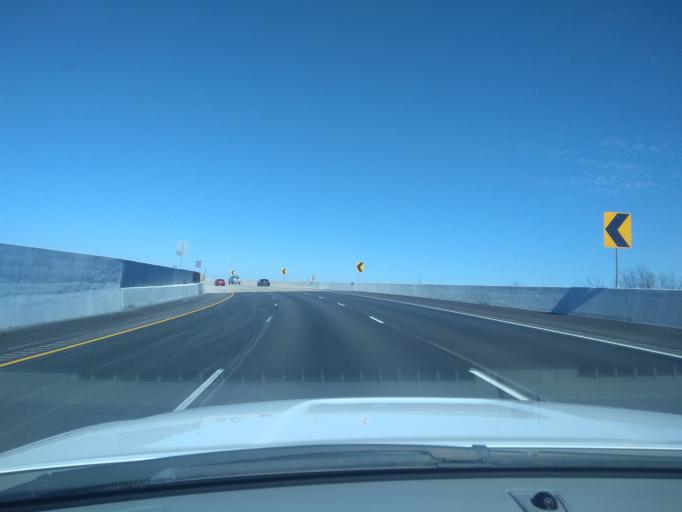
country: US
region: Arkansas
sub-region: Washington County
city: Johnson
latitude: 36.1084
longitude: -94.1704
